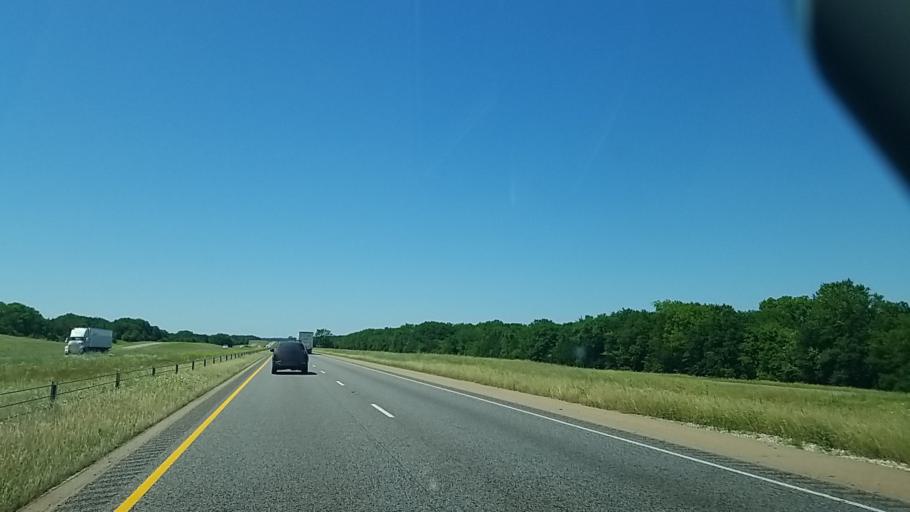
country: US
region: Texas
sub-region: Freestone County
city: Fairfield
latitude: 31.6157
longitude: -96.1568
